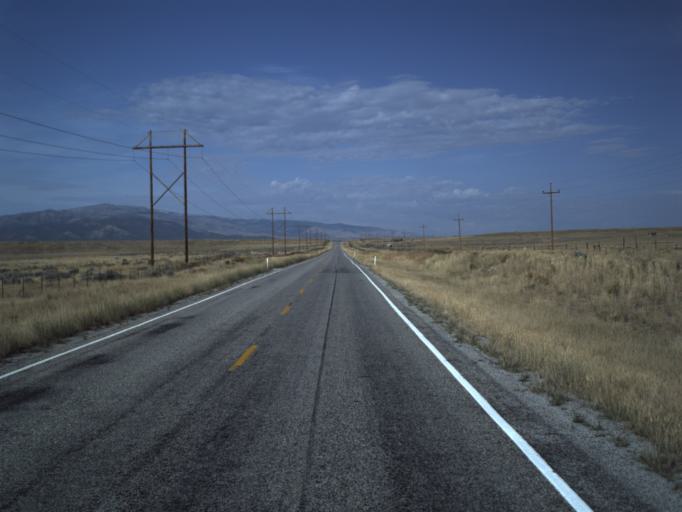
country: US
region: Idaho
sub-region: Oneida County
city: Malad City
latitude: 41.9654
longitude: -113.0412
